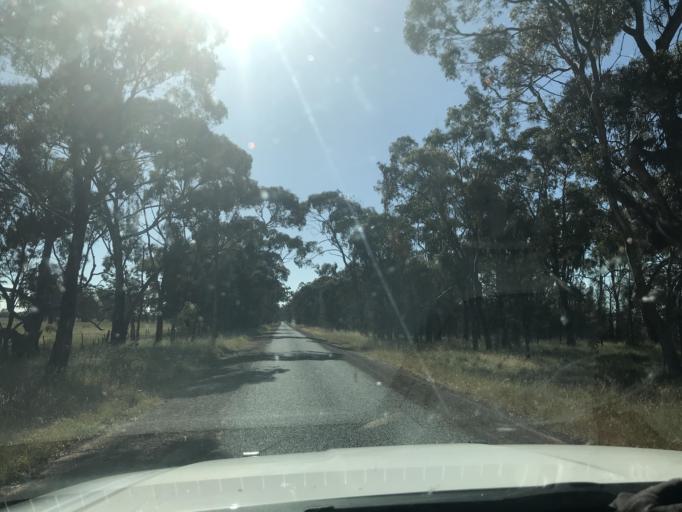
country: AU
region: Victoria
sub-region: Horsham
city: Horsham
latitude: -37.0244
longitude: 141.6971
